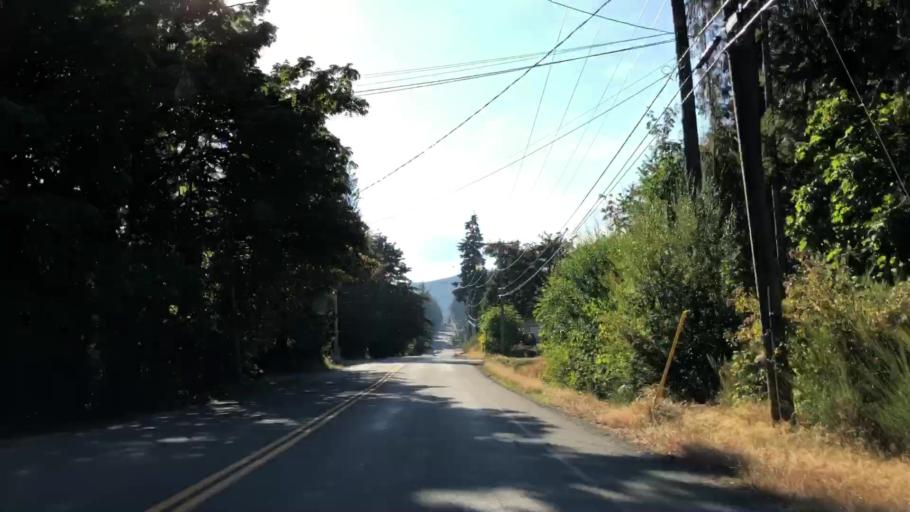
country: CA
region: British Columbia
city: North Saanich
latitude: 48.6864
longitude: -123.5727
